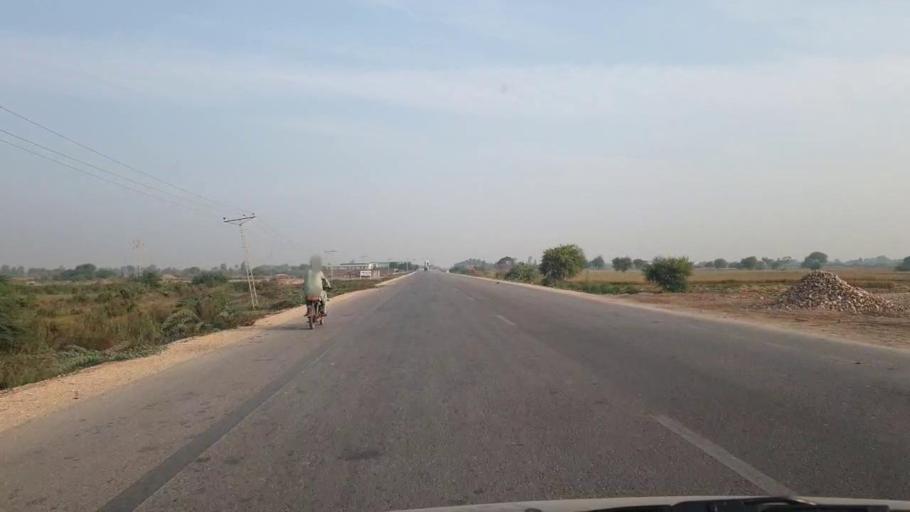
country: PK
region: Sindh
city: Badin
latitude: 24.6896
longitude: 68.8237
